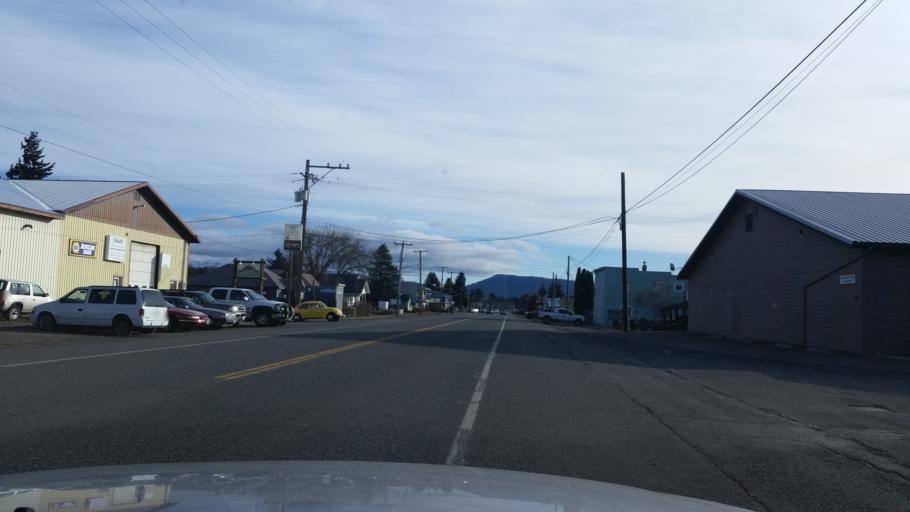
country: US
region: Washington
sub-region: Kittitas County
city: Cle Elum
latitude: 47.1934
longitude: -120.9263
